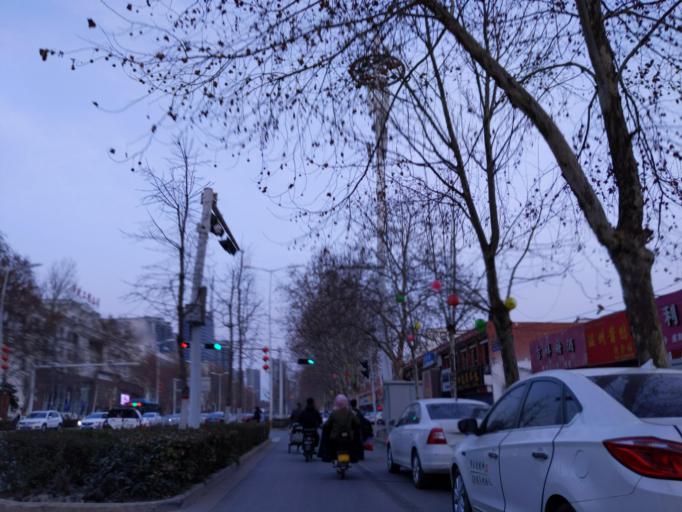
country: CN
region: Henan Sheng
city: Zhongyuanlu
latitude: 35.7804
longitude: 115.0386
